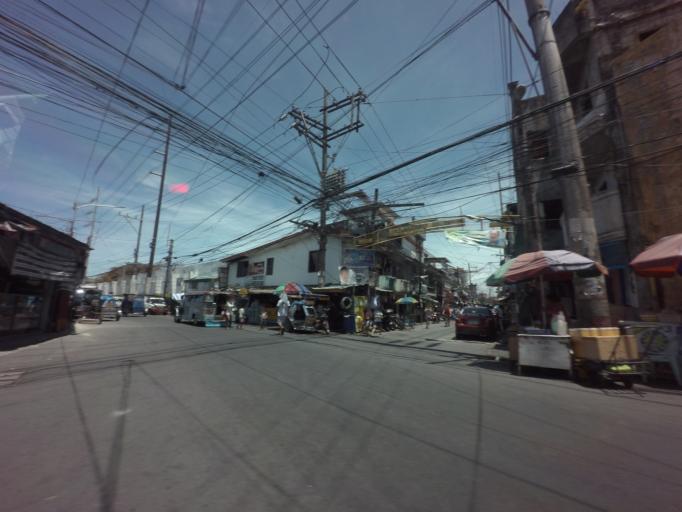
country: PH
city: Sambayanihan People's Village
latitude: 14.4892
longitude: 120.9886
